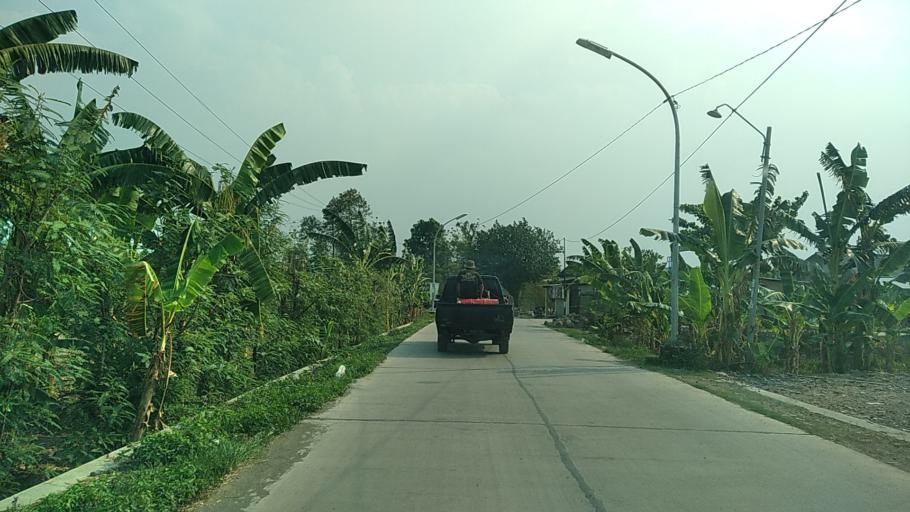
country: ID
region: Central Java
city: Mranggen
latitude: -7.0718
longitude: 110.4678
